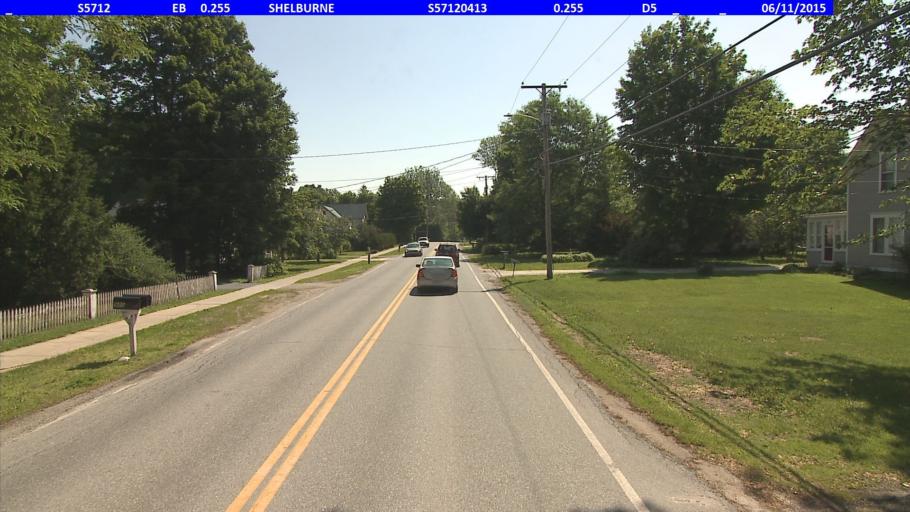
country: US
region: Vermont
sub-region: Chittenden County
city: Burlington
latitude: 44.3708
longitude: -73.2196
